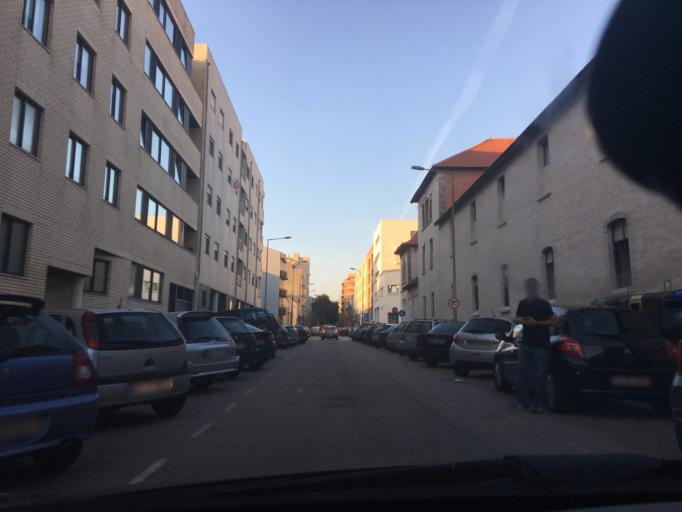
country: PT
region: Porto
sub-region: Matosinhos
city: Matosinhos
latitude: 41.1780
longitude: -8.6874
